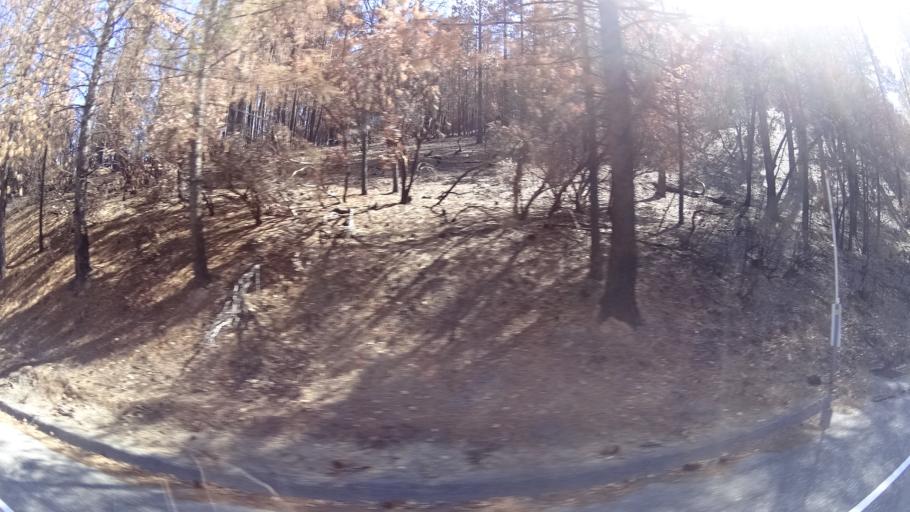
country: US
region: California
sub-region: Tehama County
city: Rancho Tehama Reserve
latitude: 39.6696
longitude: -122.7122
